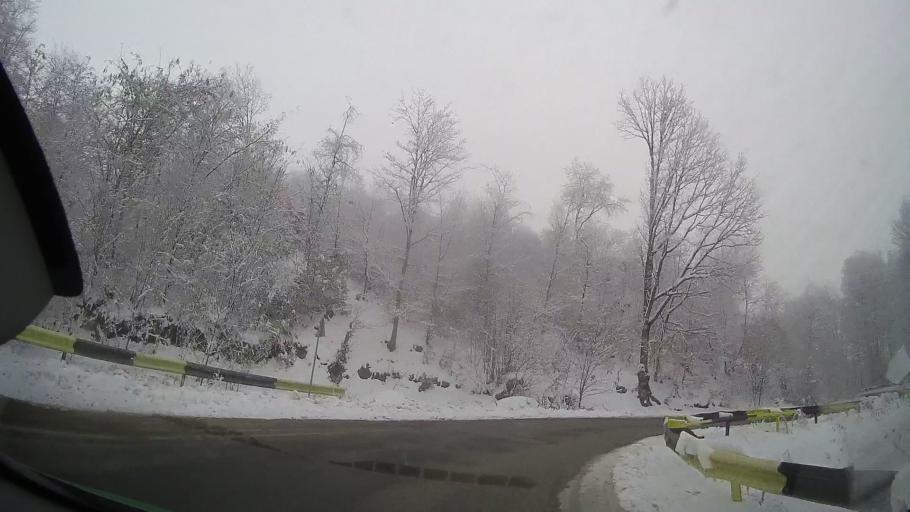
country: RO
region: Neamt
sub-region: Comuna Valea Ursului
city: Valea Ursului
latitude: 46.8426
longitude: 27.0676
